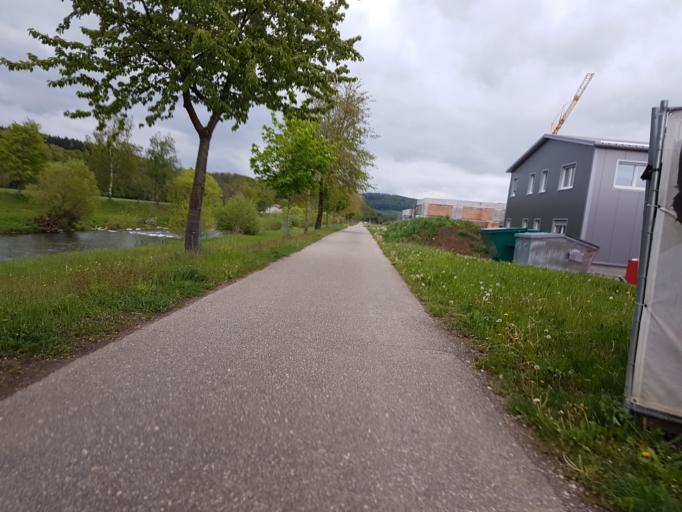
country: DE
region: Baden-Wuerttemberg
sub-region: Freiburg Region
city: Wutoschingen
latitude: 47.6396
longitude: 8.3476
